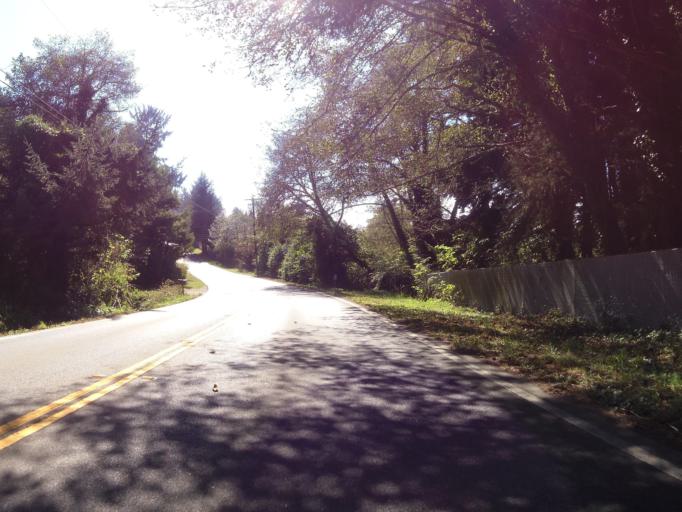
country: US
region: Oregon
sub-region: Curry County
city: Harbor
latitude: 41.9591
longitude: -124.1997
